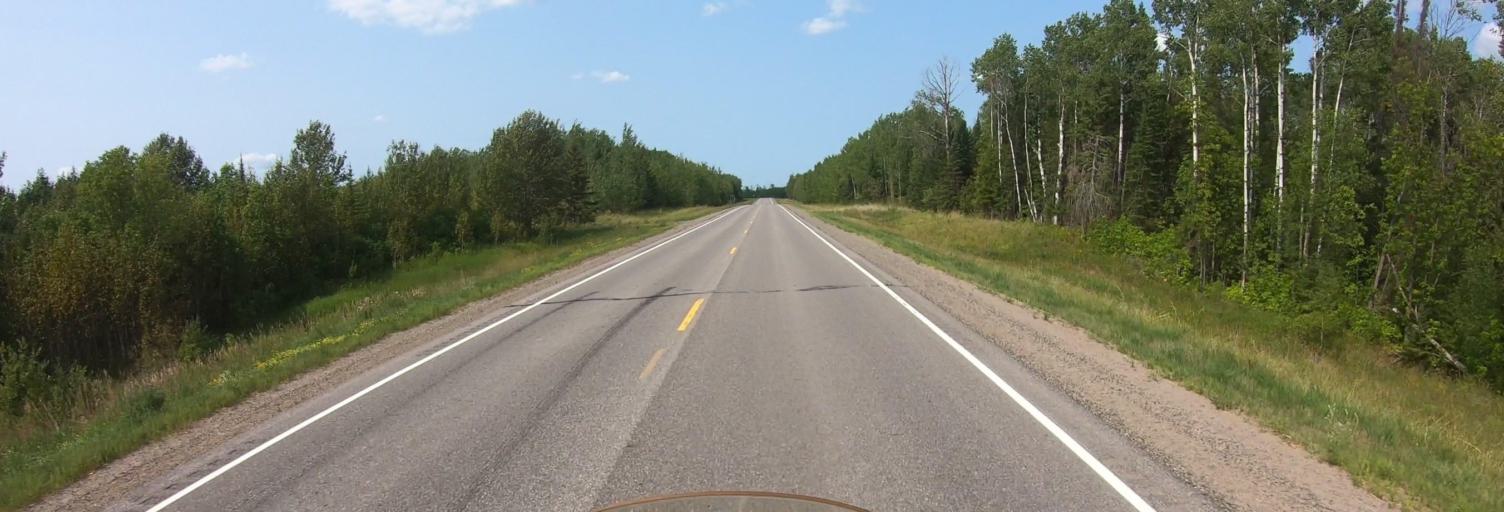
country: US
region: Minnesota
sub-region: Lake of the Woods County
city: Baudette
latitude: 48.6377
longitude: -94.1286
